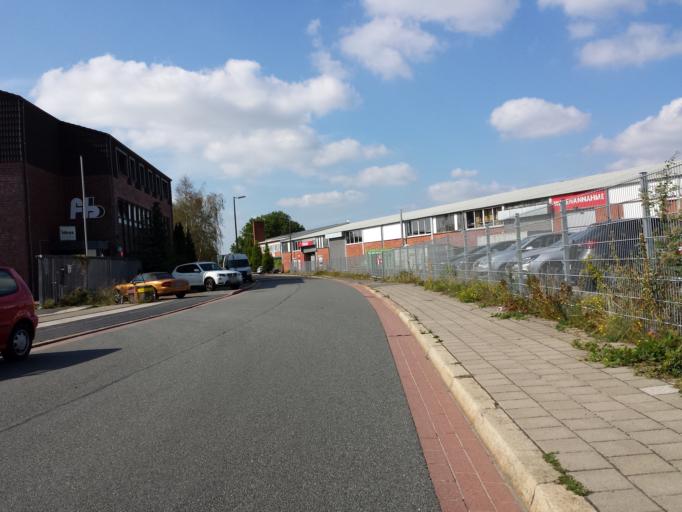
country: DE
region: Bremen
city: Bremen
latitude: 53.0799
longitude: 8.7827
